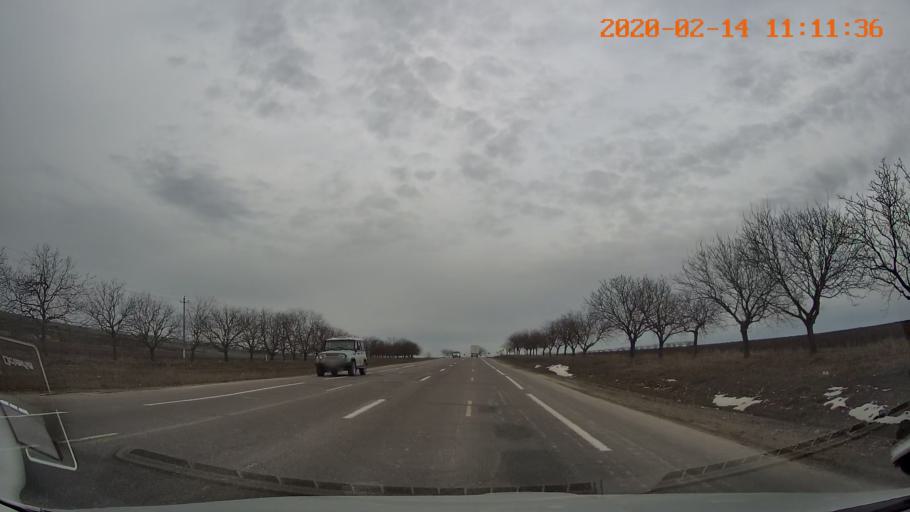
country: MD
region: Raionul Edinet
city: Edinet
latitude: 48.1984
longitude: 27.2722
